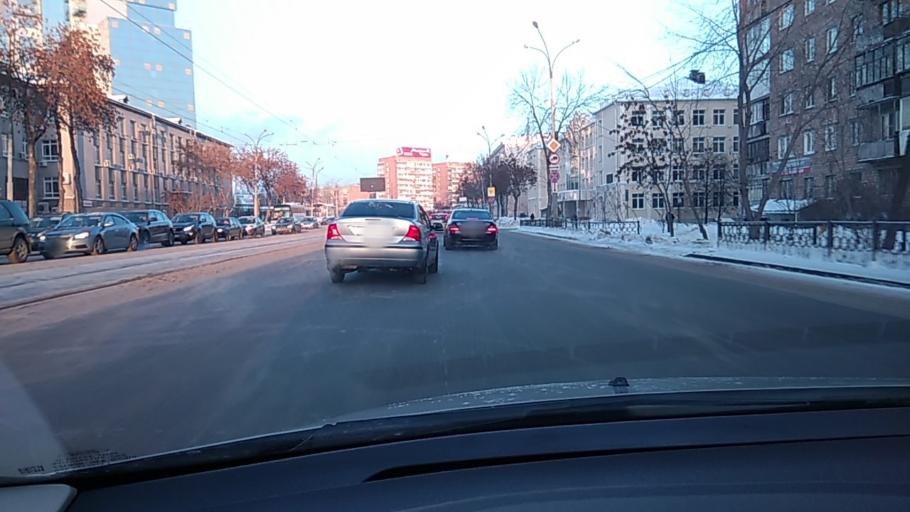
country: RU
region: Sverdlovsk
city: Yekaterinburg
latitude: 56.8539
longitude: 60.5980
